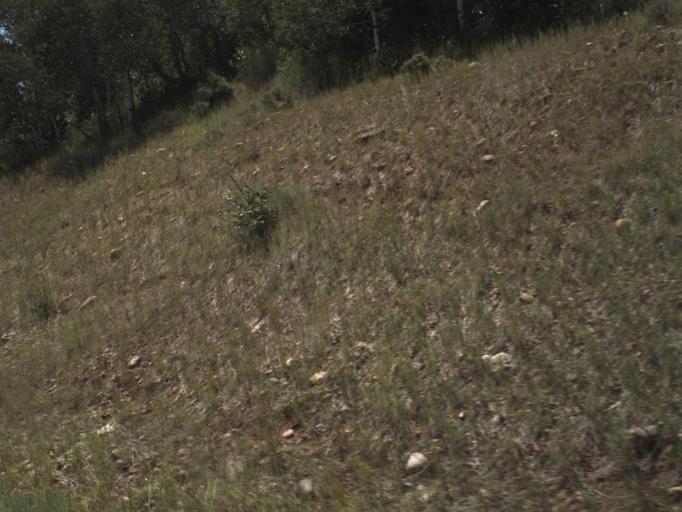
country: US
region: Utah
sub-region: Weber County
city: Wolf Creek
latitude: 41.4200
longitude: -111.5662
